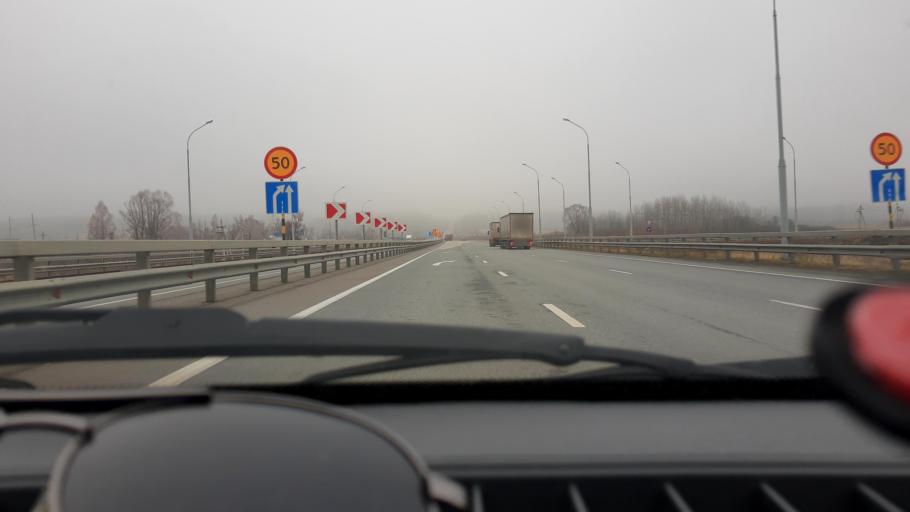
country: RU
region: Bashkortostan
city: Kabakovo
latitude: 54.6671
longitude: 56.1607
